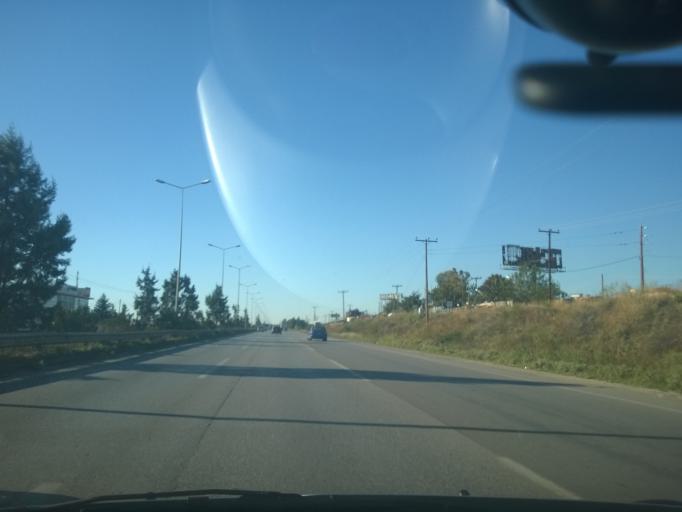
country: GR
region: Central Macedonia
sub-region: Nomos Thessalonikis
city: Thermi
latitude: 40.5535
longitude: 22.9989
